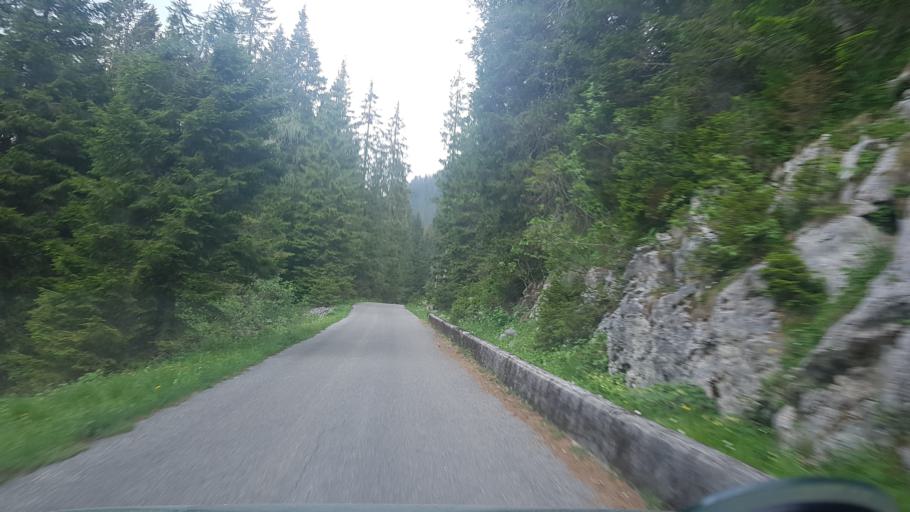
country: IT
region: Friuli Venezia Giulia
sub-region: Provincia di Udine
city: Paularo
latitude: 46.5585
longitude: 13.1867
